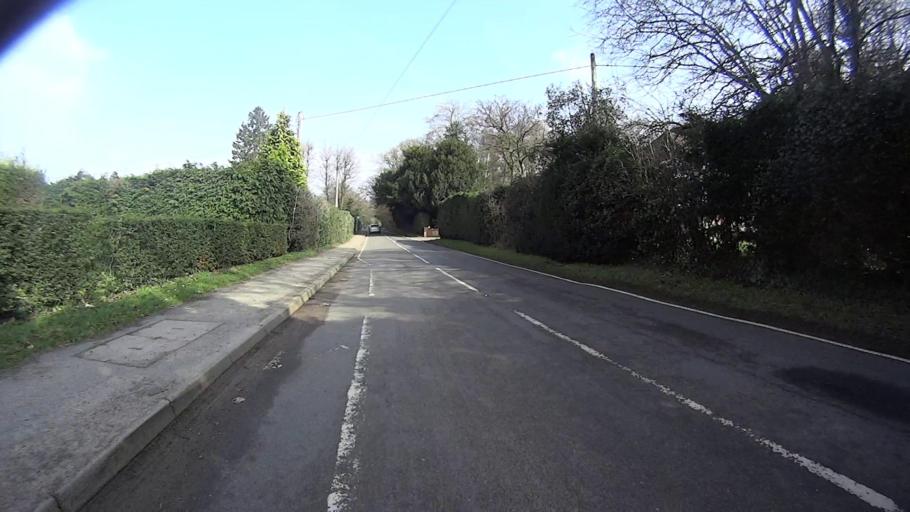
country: GB
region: England
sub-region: Surrey
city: Mickleham
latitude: 51.2482
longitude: -0.2998
